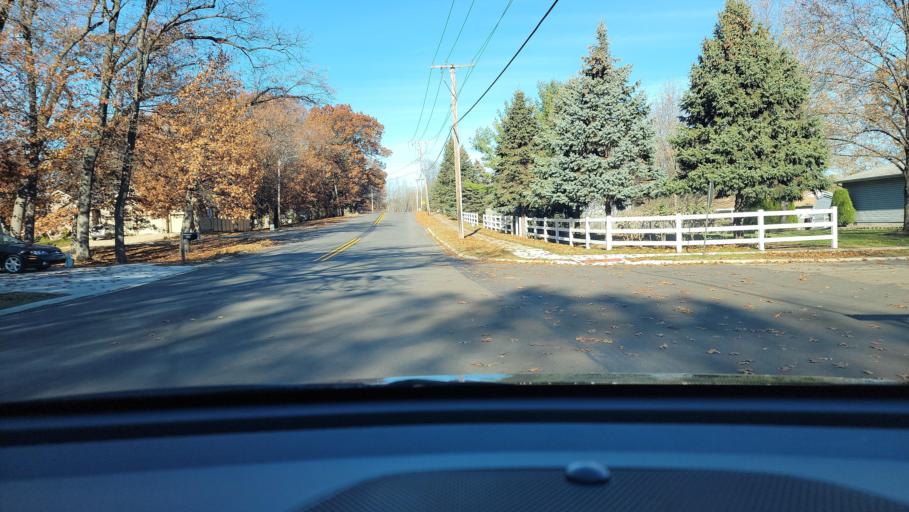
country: US
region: Indiana
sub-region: Porter County
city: Portage
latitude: 41.5877
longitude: -87.1978
